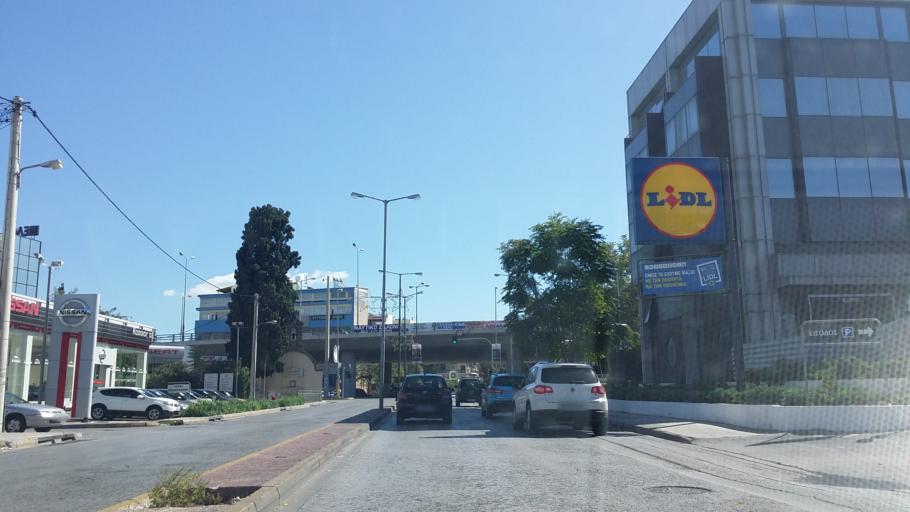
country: GR
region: Attica
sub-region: Nomarchia Athinas
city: Peristeri
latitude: 38.0092
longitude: 23.7140
